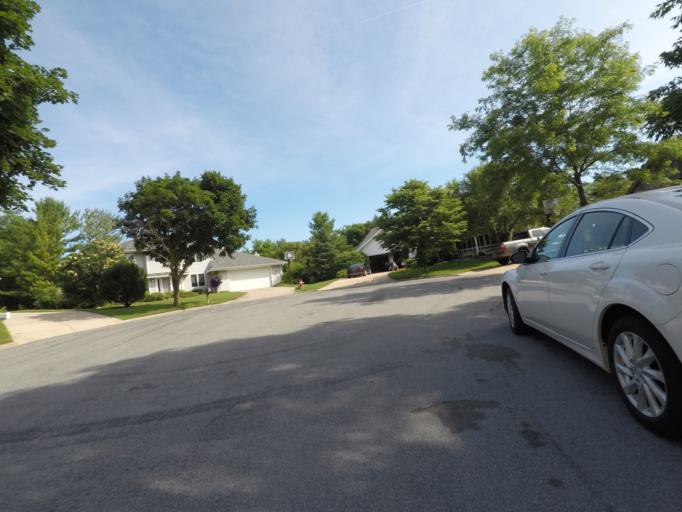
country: US
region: Wisconsin
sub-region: Dane County
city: Middleton
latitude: 43.0788
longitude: -89.4944
